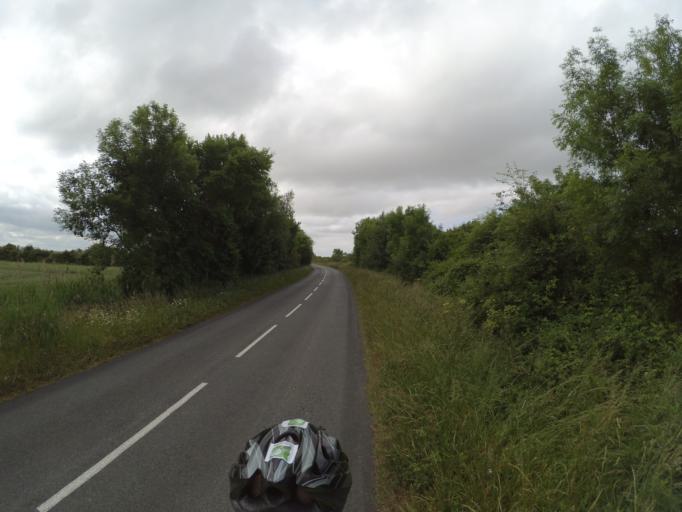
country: FR
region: Poitou-Charentes
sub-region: Departement de la Charente-Maritime
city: Yves
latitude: 46.0369
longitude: -1.0454
